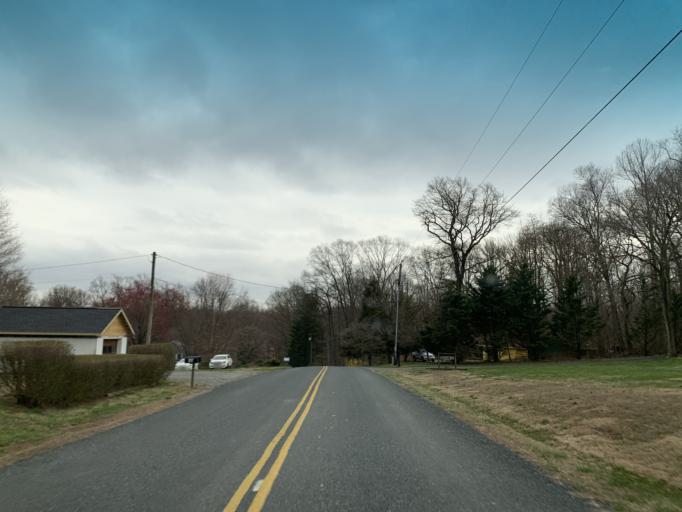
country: US
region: Maryland
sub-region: Harford County
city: Aberdeen
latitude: 39.5249
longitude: -76.2097
